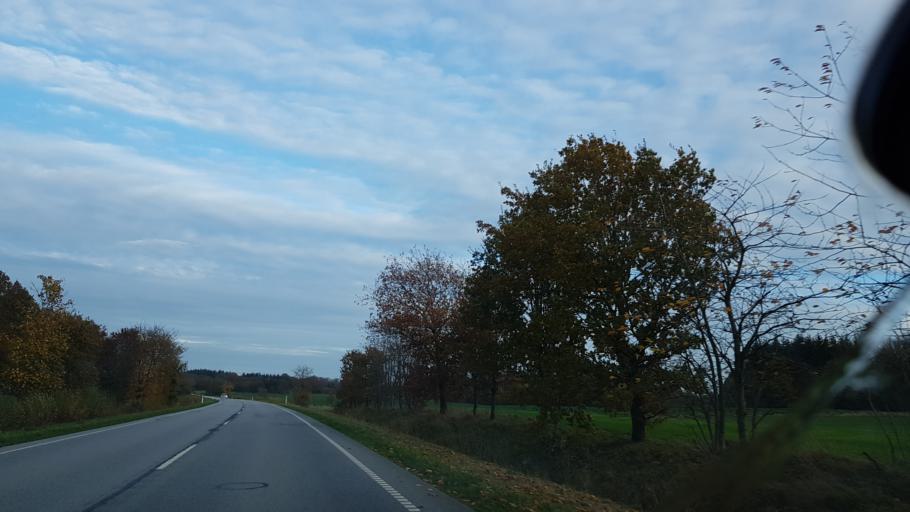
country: DK
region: South Denmark
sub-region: Haderslev Kommune
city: Haderslev
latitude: 55.2937
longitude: 9.3989
